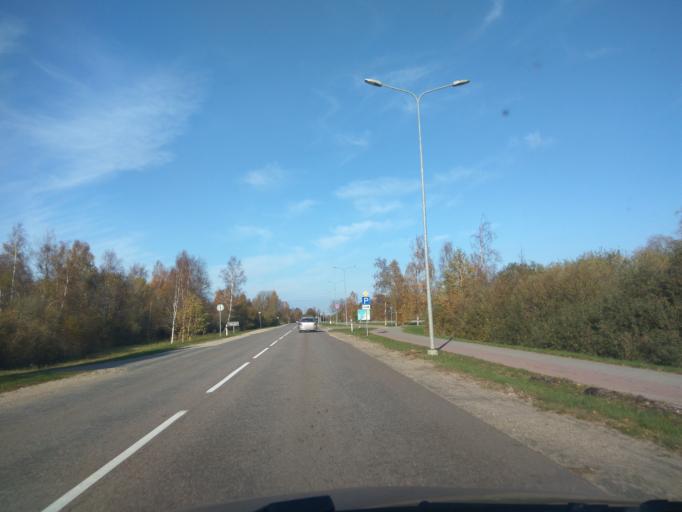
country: LV
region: Ventspils
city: Ventspils
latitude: 57.3579
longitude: 21.5635
